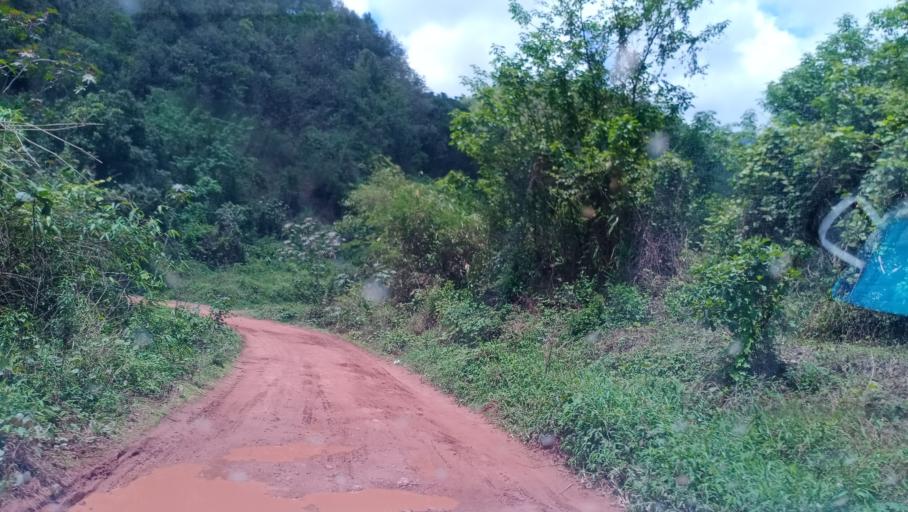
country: CN
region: Yunnan
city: Menglie
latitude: 22.1427
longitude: 101.7760
